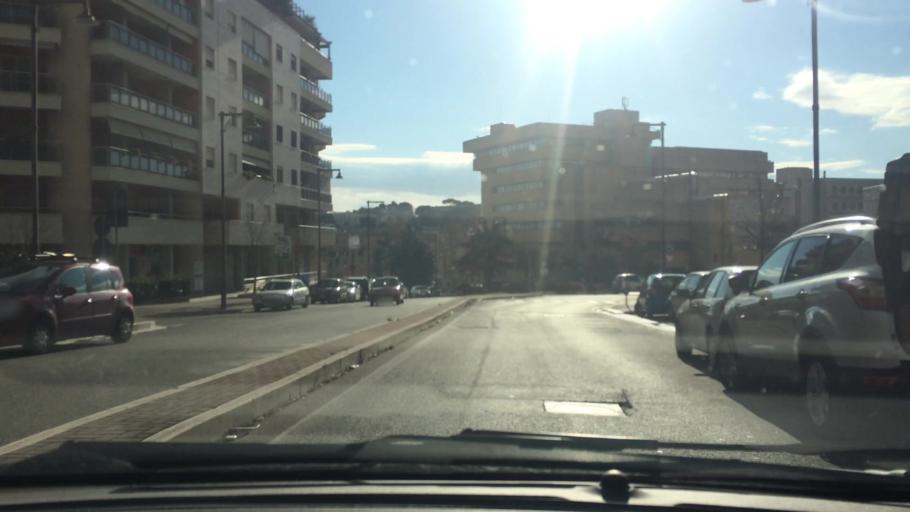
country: IT
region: Basilicate
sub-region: Provincia di Matera
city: Matera
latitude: 40.6680
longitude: 16.5999
